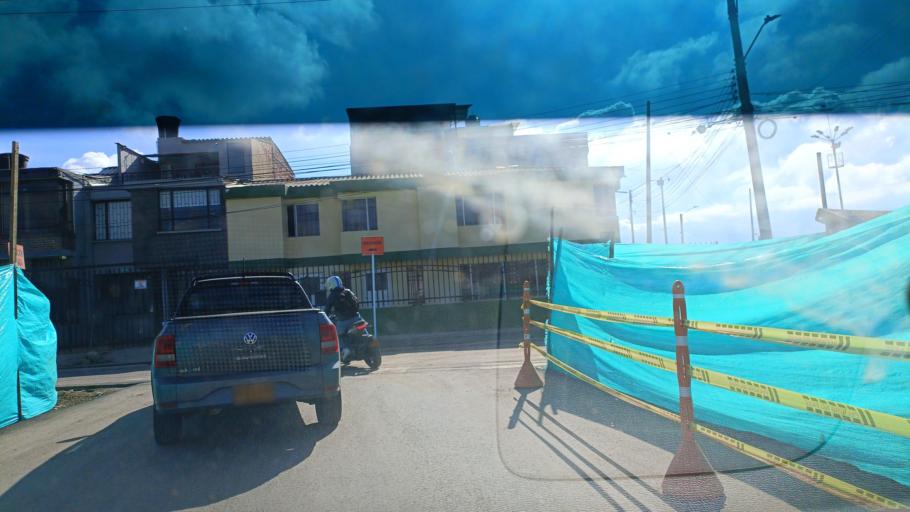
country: CO
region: Cundinamarca
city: Cajica
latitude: 4.9109
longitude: -74.0251
